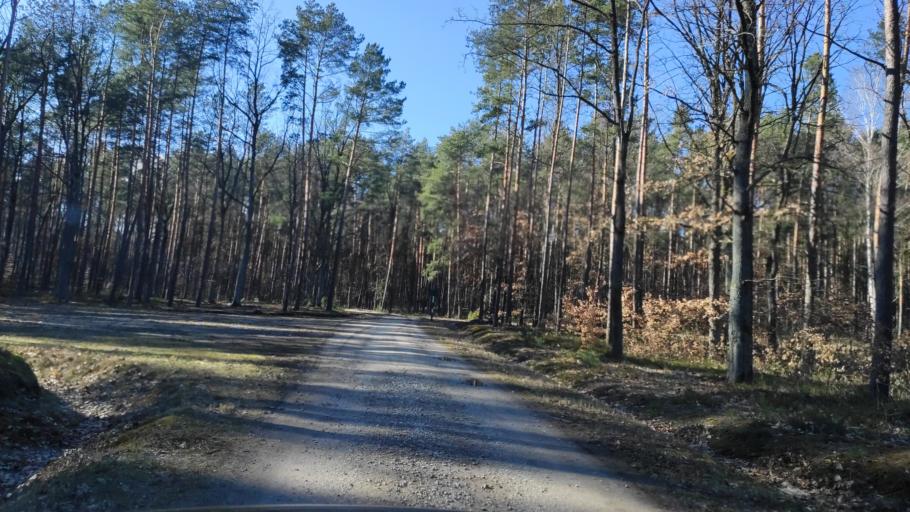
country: PL
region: Masovian Voivodeship
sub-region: Powiat radomski
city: Jastrzebia
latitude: 51.4753
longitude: 21.2643
